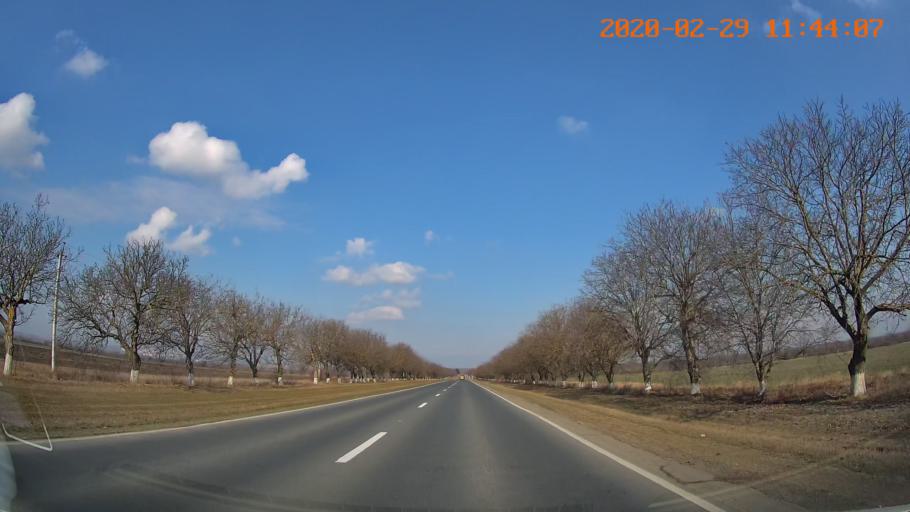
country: MD
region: Rezina
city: Saharna
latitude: 47.7065
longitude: 29.0010
